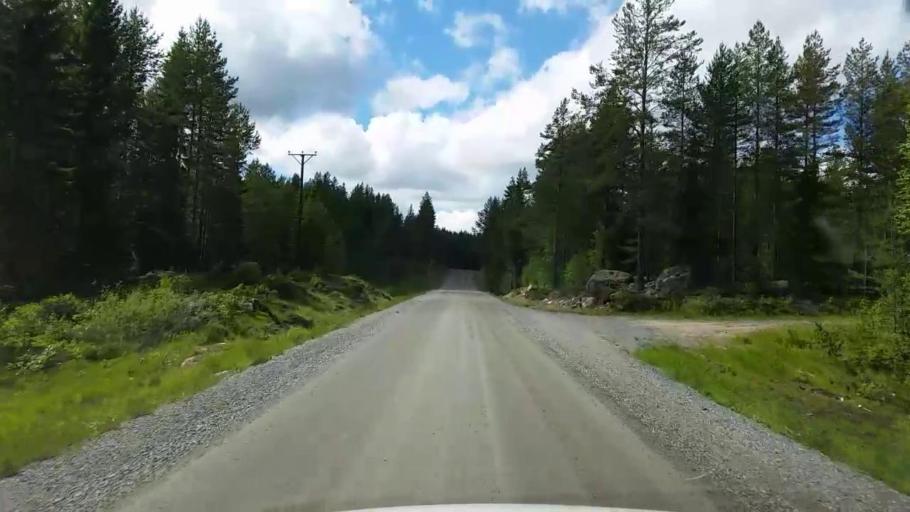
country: SE
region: Gaevleborg
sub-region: Bollnas Kommun
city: Vittsjo
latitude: 61.0684
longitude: 16.2903
